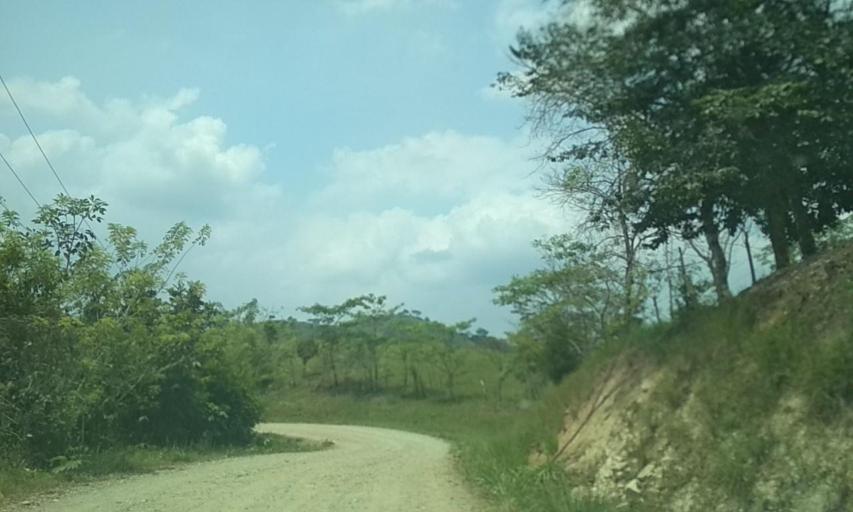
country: MX
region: Tabasco
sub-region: Huimanguillo
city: Francisco Rueda
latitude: 17.6262
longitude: -93.8181
